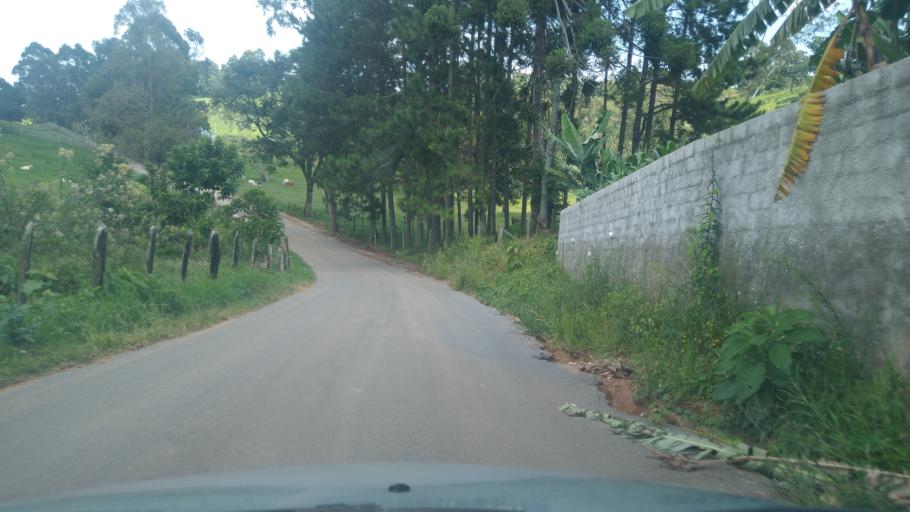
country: BR
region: Minas Gerais
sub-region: Extrema
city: Extrema
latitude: -22.7286
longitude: -46.3087
